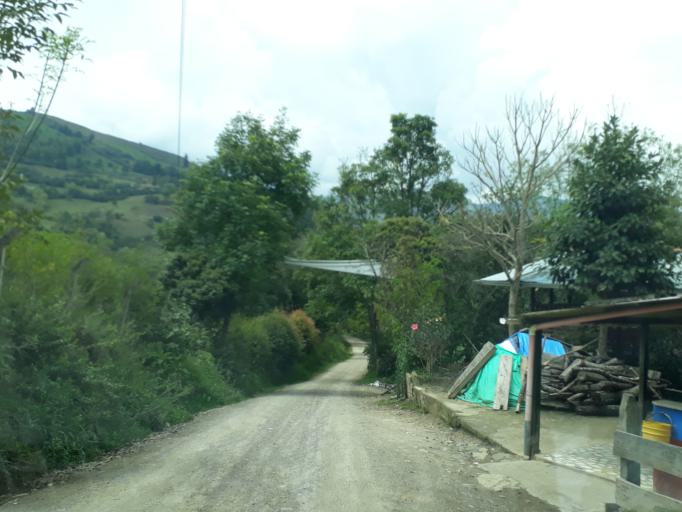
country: CO
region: Cundinamarca
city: Macheta
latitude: 5.0909
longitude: -73.5722
